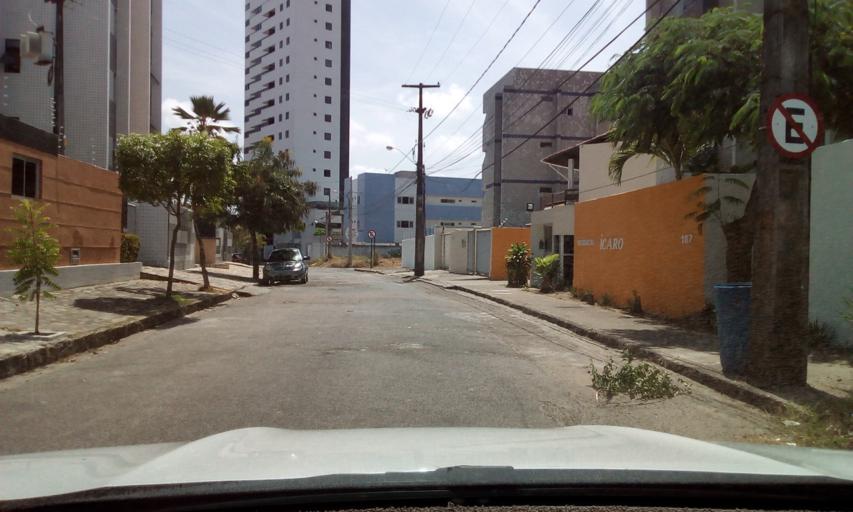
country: BR
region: Paraiba
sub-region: Joao Pessoa
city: Joao Pessoa
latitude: -7.0941
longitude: -34.8452
